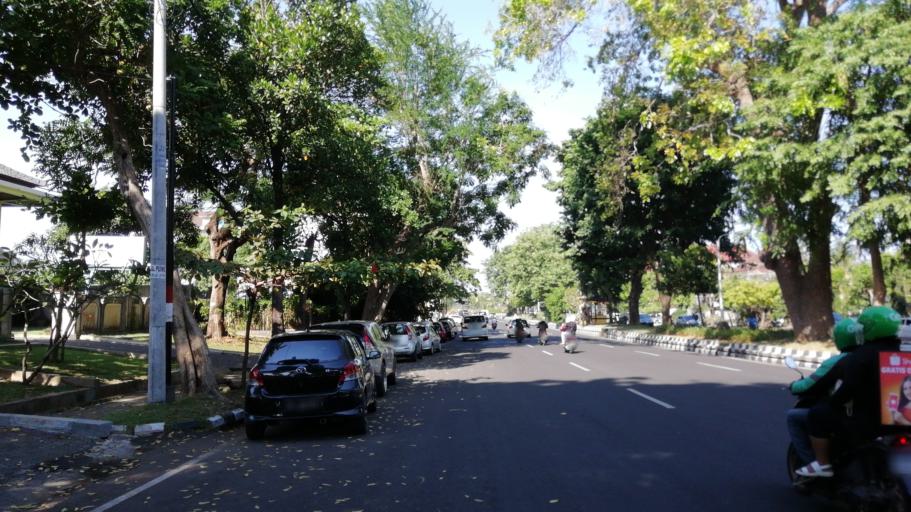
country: ID
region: Bali
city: Banjar Batanpoh
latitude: -8.6734
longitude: 115.2427
